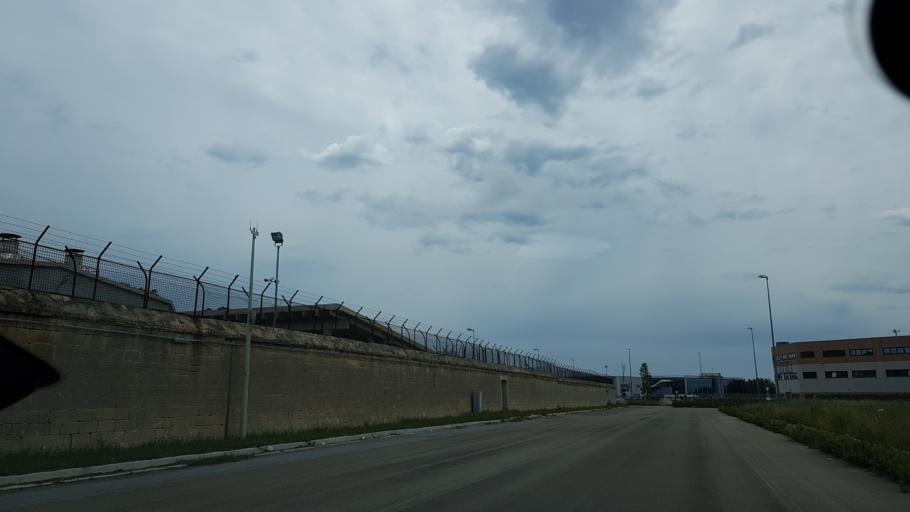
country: IT
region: Apulia
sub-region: Provincia di Brindisi
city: Brindisi
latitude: 40.6343
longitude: 17.9569
